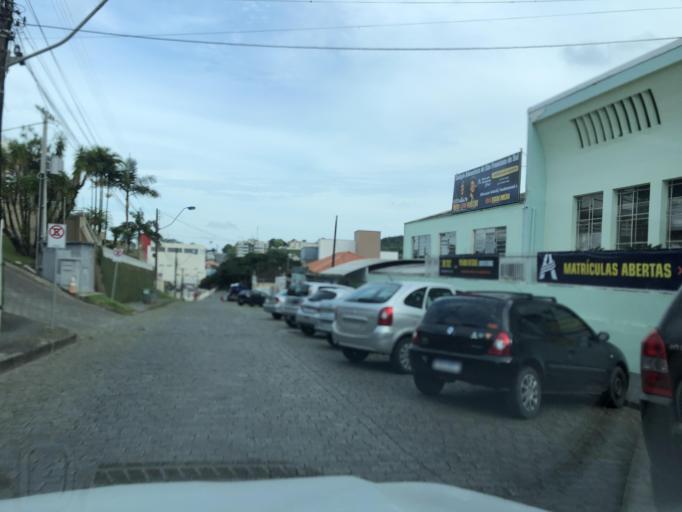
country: BR
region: Santa Catarina
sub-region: Sao Francisco Do Sul
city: Sao Francisco do Sul
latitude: -26.2475
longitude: -48.6390
